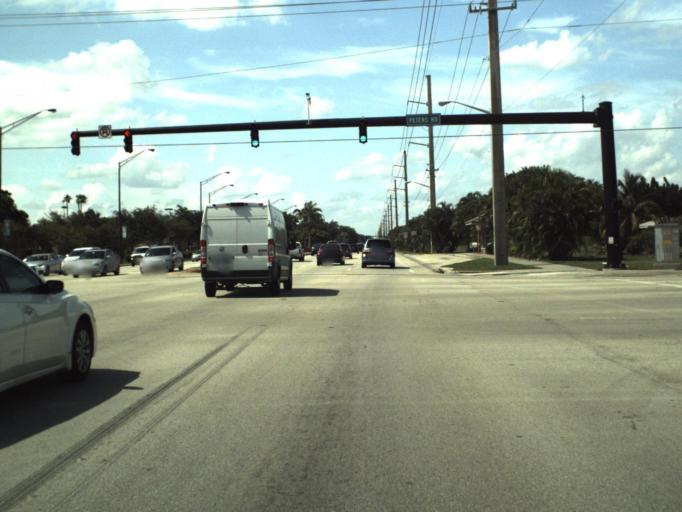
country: US
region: Florida
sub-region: Broward County
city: Pine Island Ridge
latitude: 26.1053
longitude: -80.2500
